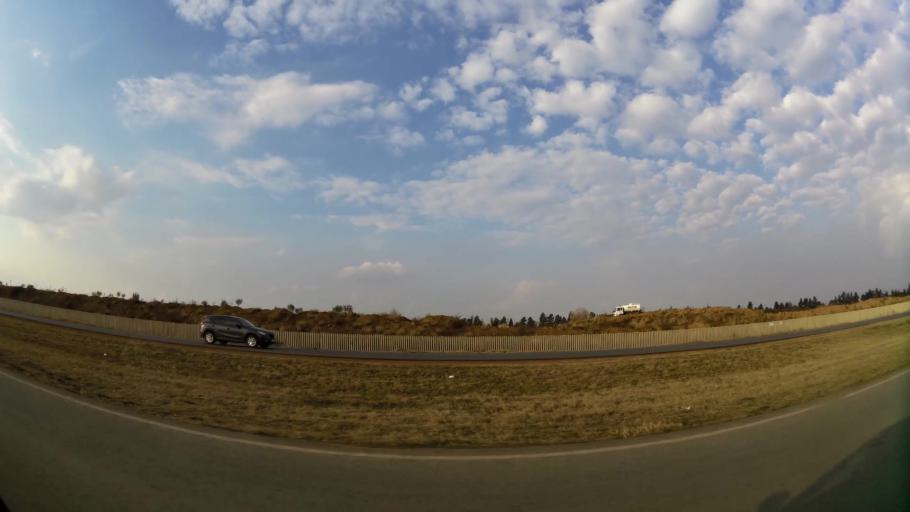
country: ZA
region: Gauteng
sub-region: Sedibeng District Municipality
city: Vereeniging
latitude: -26.6426
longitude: 27.8738
